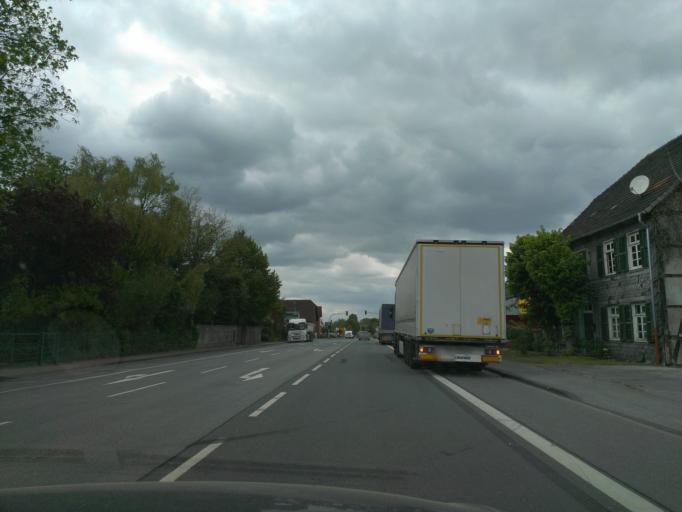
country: DE
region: North Rhine-Westphalia
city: Erwitte
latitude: 51.6116
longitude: 8.3348
